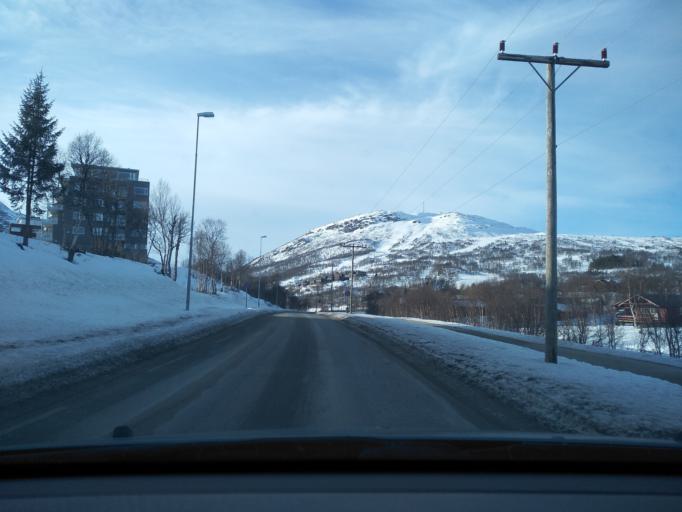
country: NO
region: Aust-Agder
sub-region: Bykle
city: Hovden
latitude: 59.5674
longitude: 7.3627
